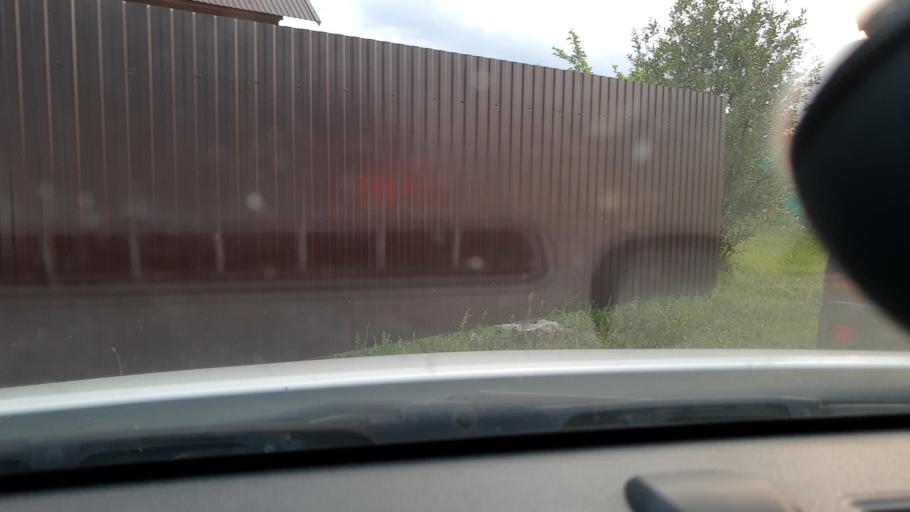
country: RU
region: Bashkortostan
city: Kabakovo
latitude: 54.4412
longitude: 55.9130
